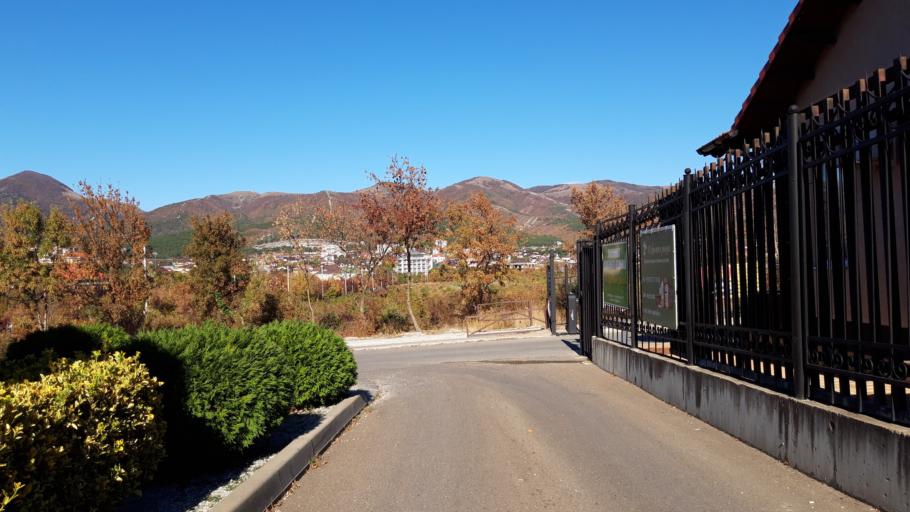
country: RU
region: Krasnodarskiy
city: Kabardinka
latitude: 44.6427
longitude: 37.9357
